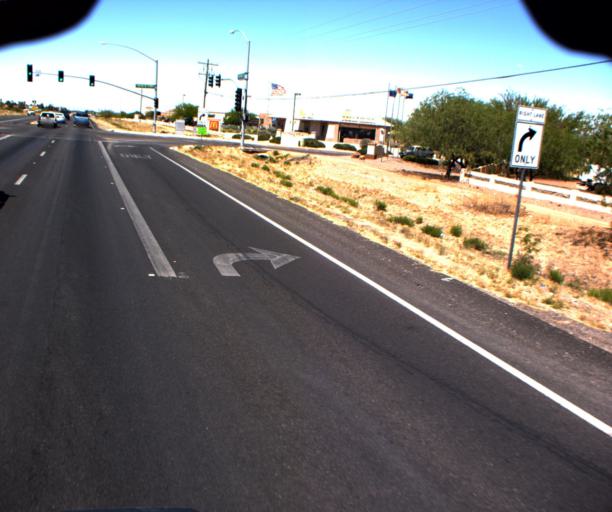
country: US
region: Arizona
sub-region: Cochise County
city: Sierra Vista Southeast
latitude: 31.5037
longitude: -110.2573
